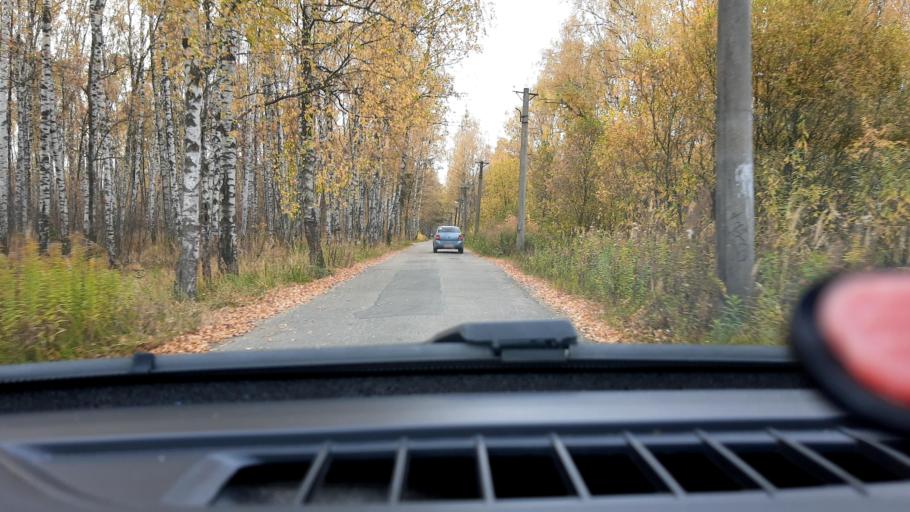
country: RU
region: Nizjnij Novgorod
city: Gorbatovka
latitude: 56.2875
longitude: 43.8303
